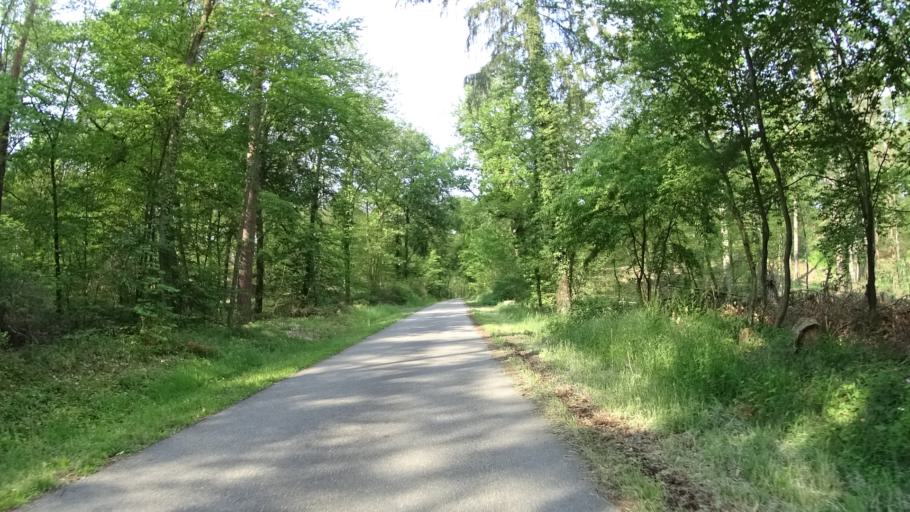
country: DE
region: Baden-Wuerttemberg
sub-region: Karlsruhe Region
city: Walldorf
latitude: 49.3234
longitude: 8.6191
